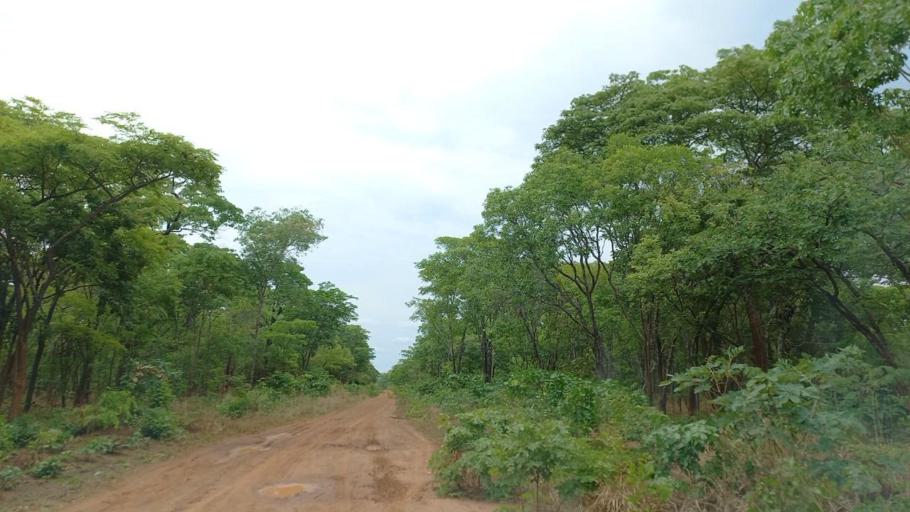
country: ZM
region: North-Western
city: Kalengwa
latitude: -13.5764
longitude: 24.9708
